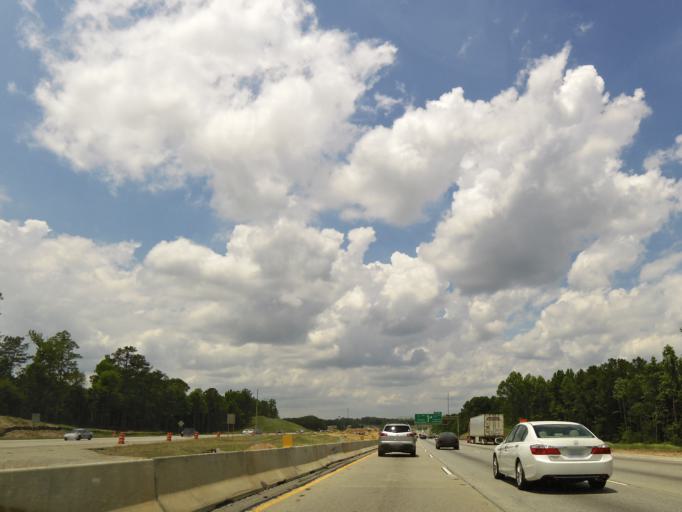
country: US
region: Georgia
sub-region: Henry County
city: Stockbridge
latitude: 33.5323
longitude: -84.2593
